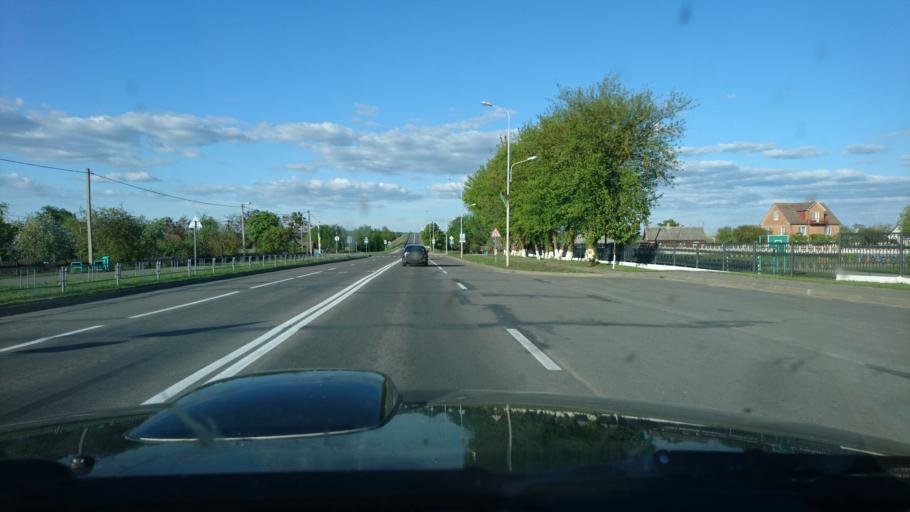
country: BY
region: Brest
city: Ivatsevichy
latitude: 52.7161
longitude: 25.3517
